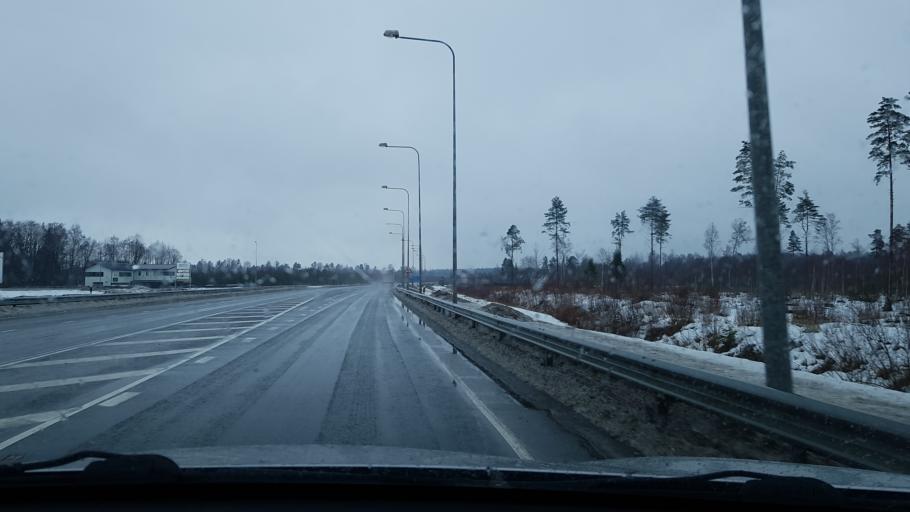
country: EE
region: Raplamaa
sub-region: Kohila vald
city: Kohila
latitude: 59.1688
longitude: 24.7718
